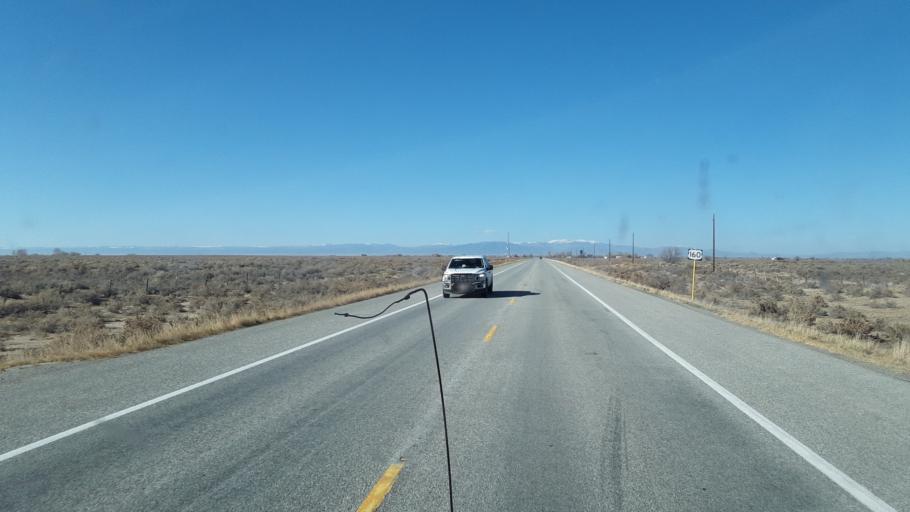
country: US
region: Colorado
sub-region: Alamosa County
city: Alamosa East
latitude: 37.4745
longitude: -105.7115
